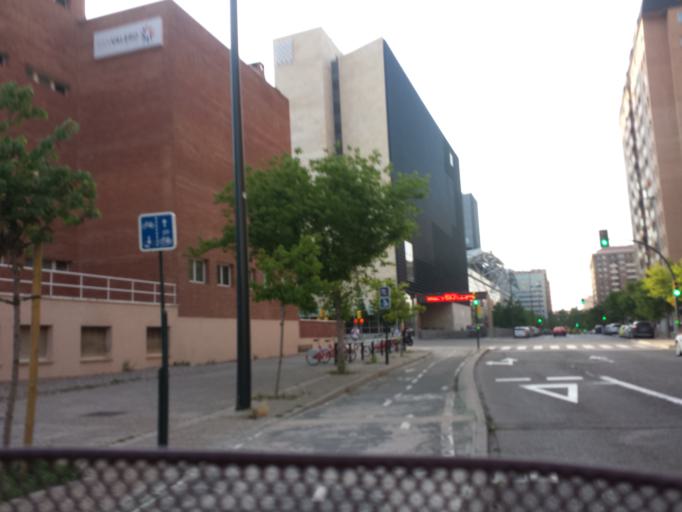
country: ES
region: Aragon
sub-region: Provincia de Zaragoza
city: Delicias
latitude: 41.6385
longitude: -0.9075
